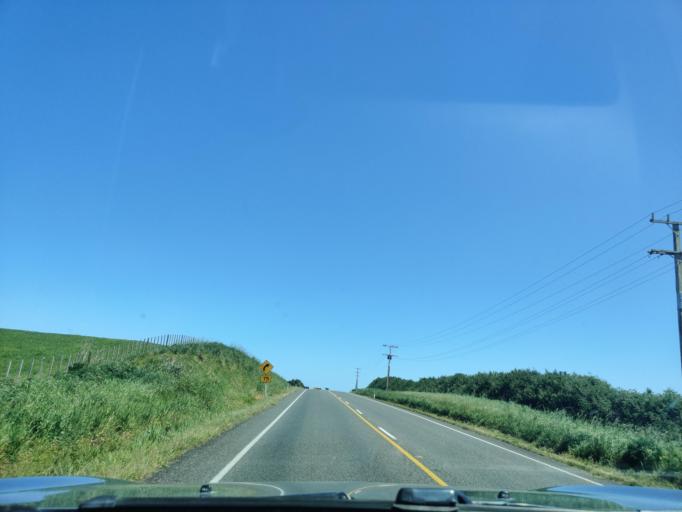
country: NZ
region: Taranaki
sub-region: South Taranaki District
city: Patea
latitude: -39.7469
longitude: 174.5022
